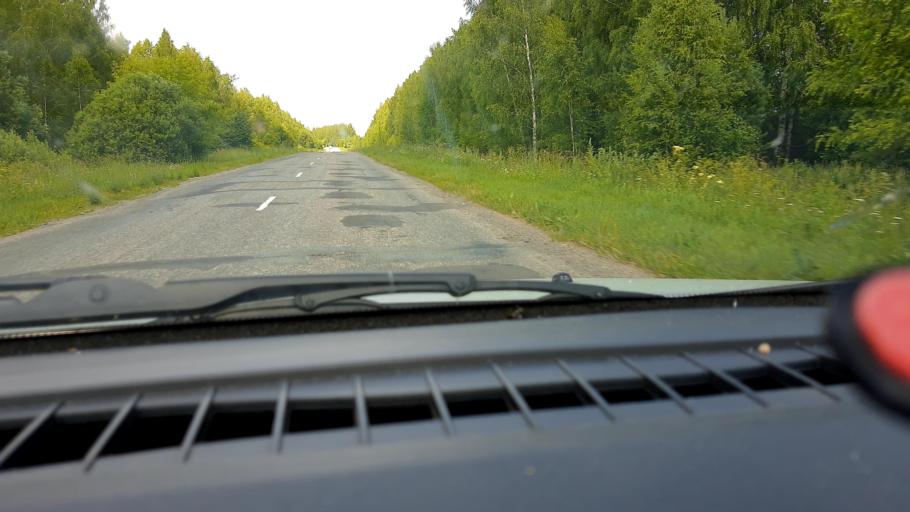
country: RU
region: Nizjnij Novgorod
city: Sharanga
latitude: 57.1097
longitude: 46.5277
